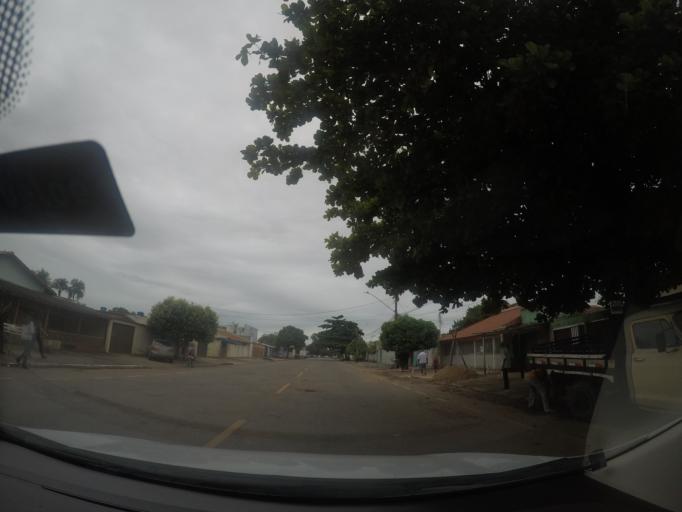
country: BR
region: Goias
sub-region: Goiania
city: Goiania
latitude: -16.6836
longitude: -49.3298
